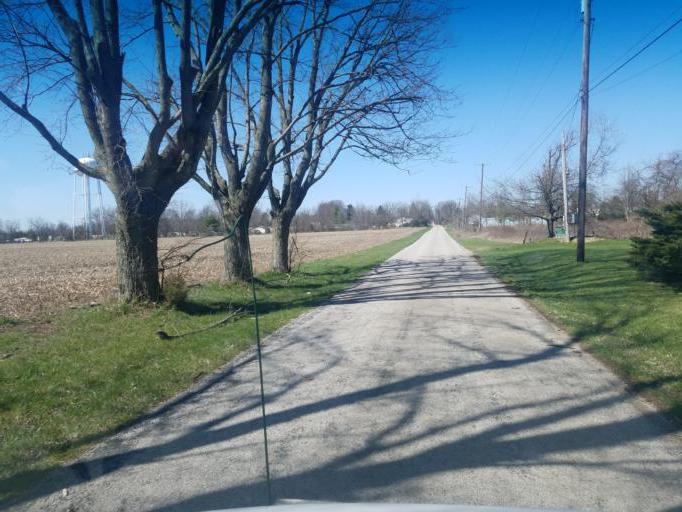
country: US
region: Ohio
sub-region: Morrow County
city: Cardington
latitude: 40.4939
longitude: -82.9020
